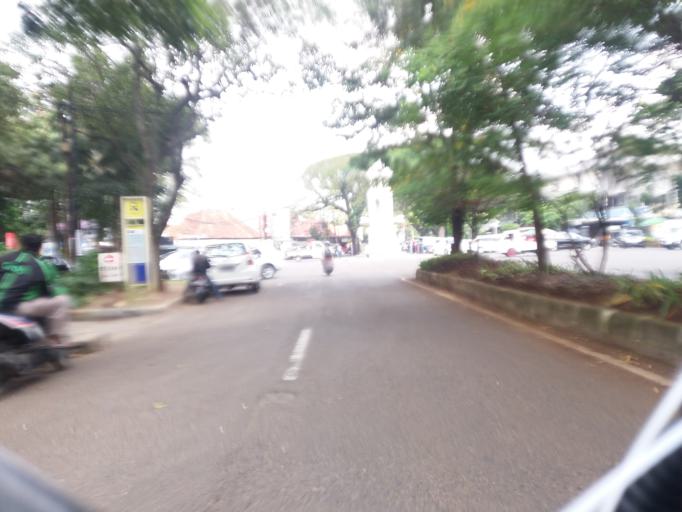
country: ID
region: West Java
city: Bandung
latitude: -6.9045
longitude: 107.6226
